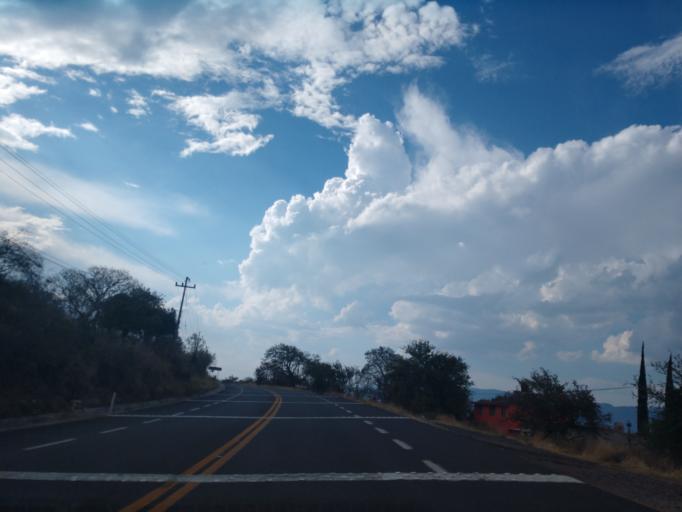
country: MX
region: Jalisco
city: Ajijic
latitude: 20.1893
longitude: -103.2554
